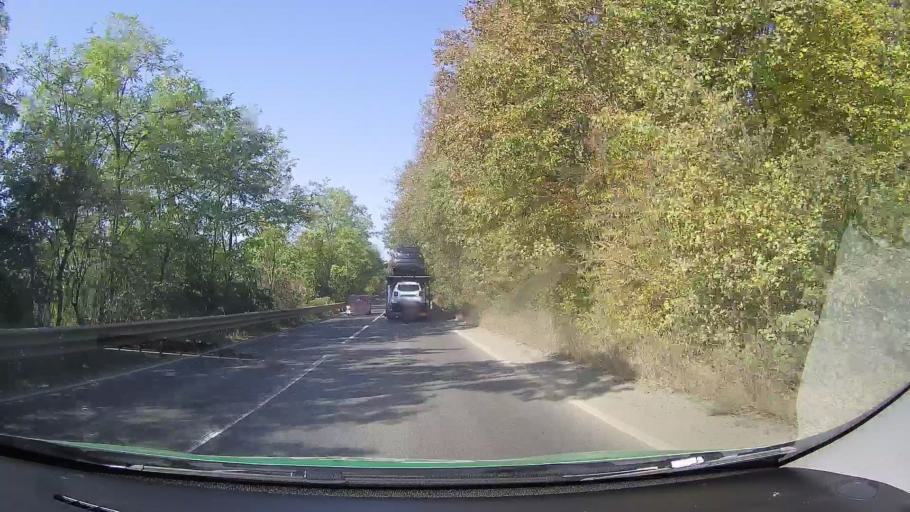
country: RO
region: Arad
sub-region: Comuna Bata
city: Bata
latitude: 46.0730
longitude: 22.0367
